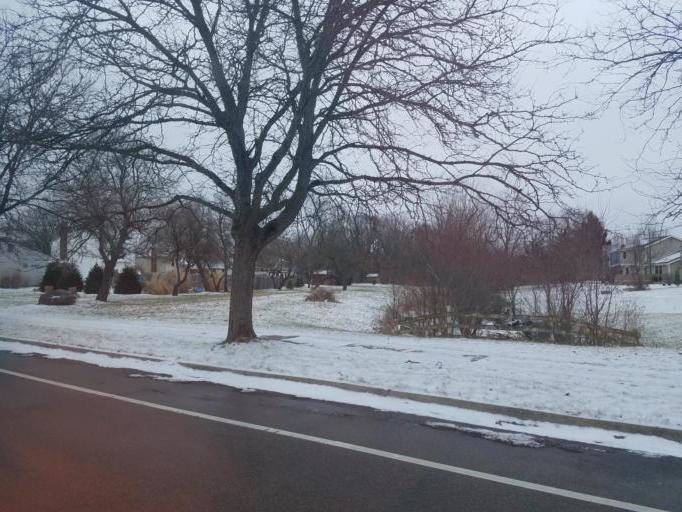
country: US
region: Ohio
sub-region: Delaware County
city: Powell
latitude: 40.1227
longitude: -83.0627
